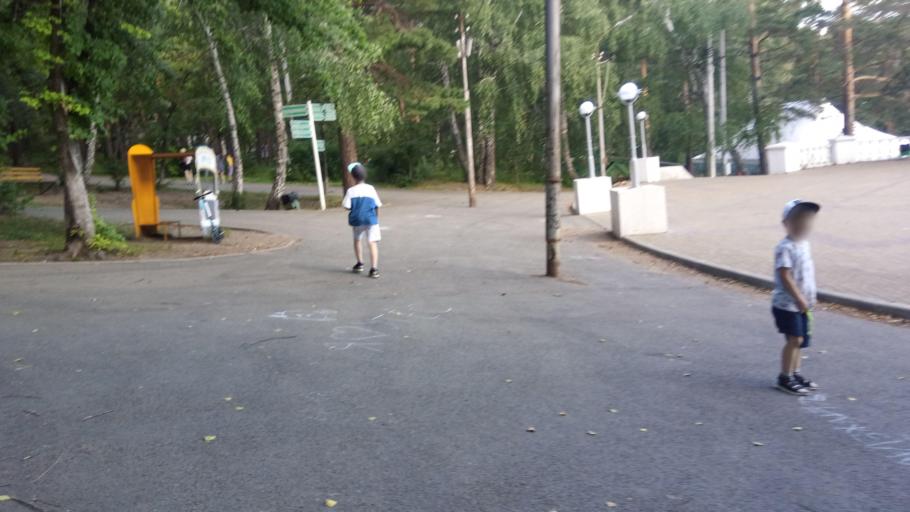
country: RU
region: Chelyabinsk
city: Chebarkul'
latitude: 55.0158
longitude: 60.3146
